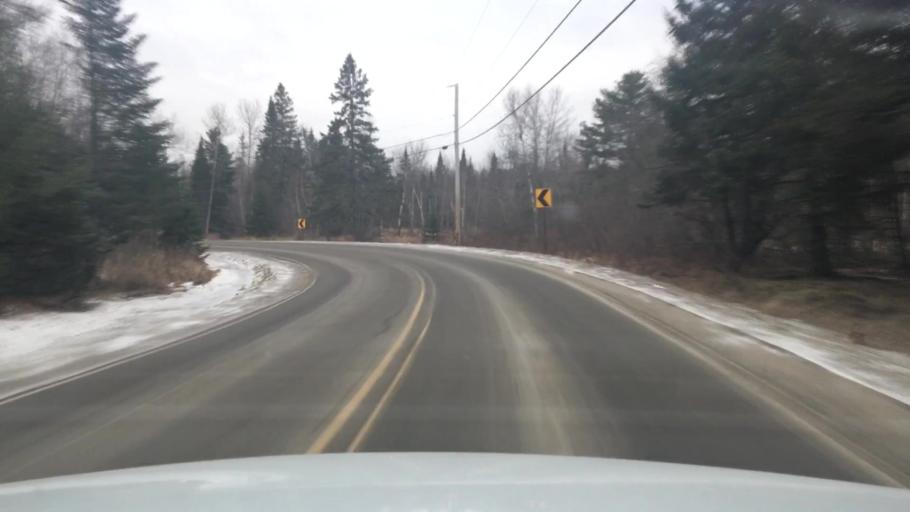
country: US
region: Maine
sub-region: Hancock County
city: Hancock
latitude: 44.5356
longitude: -68.3298
